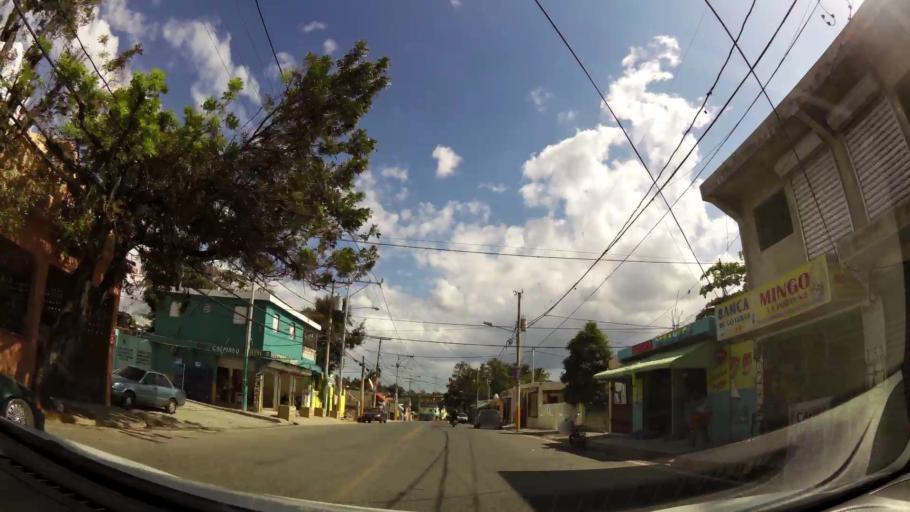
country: DO
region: Nacional
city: Ensanche Luperon
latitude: 18.5386
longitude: -69.8997
